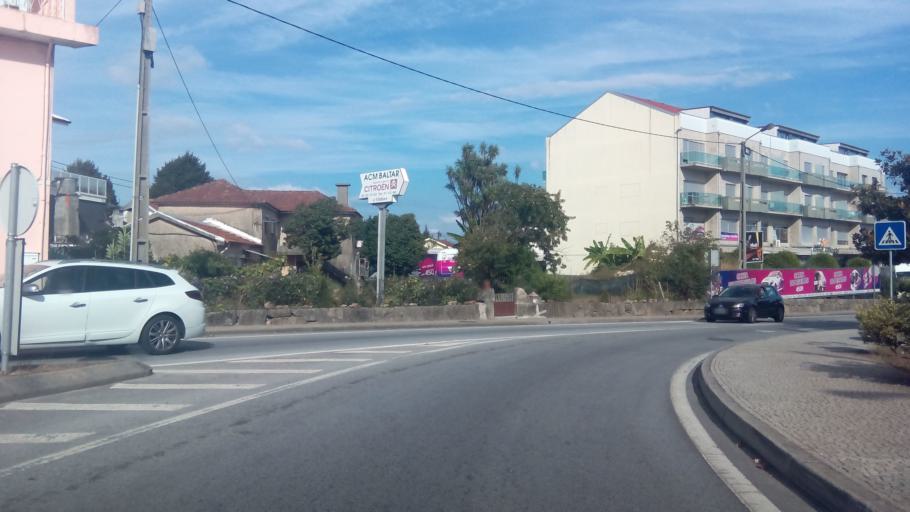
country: PT
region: Porto
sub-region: Paredes
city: Baltar
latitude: 41.1926
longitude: -8.3882
